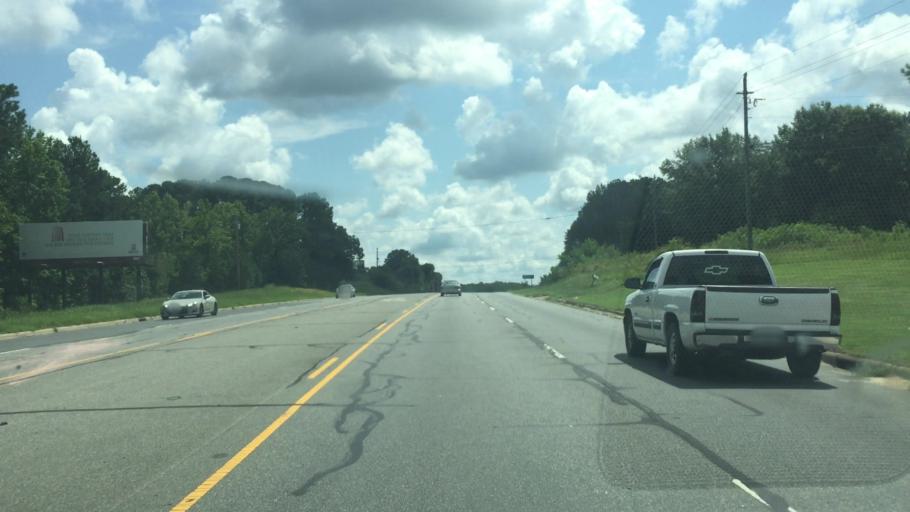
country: US
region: North Carolina
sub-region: Anson County
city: Wadesboro
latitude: 34.9636
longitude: -80.0307
